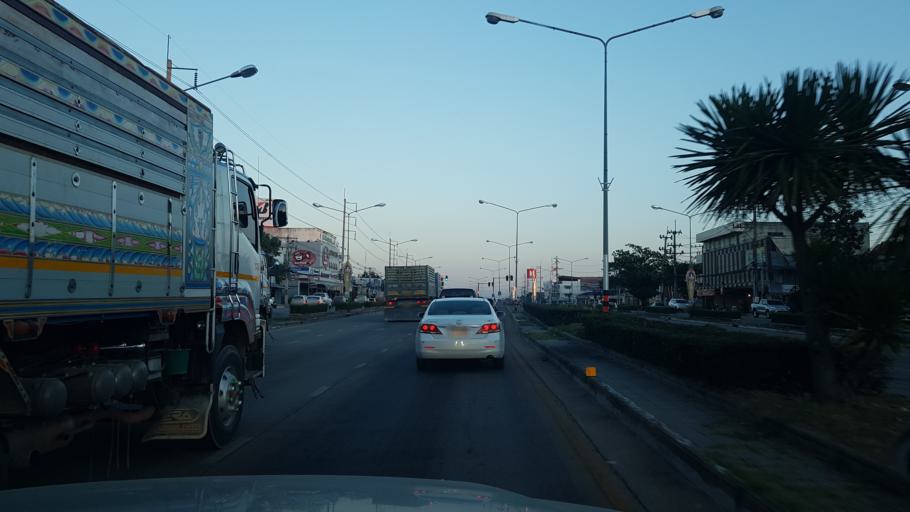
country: TH
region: Khon Kaen
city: Chum Phae
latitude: 16.5419
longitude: 102.1067
